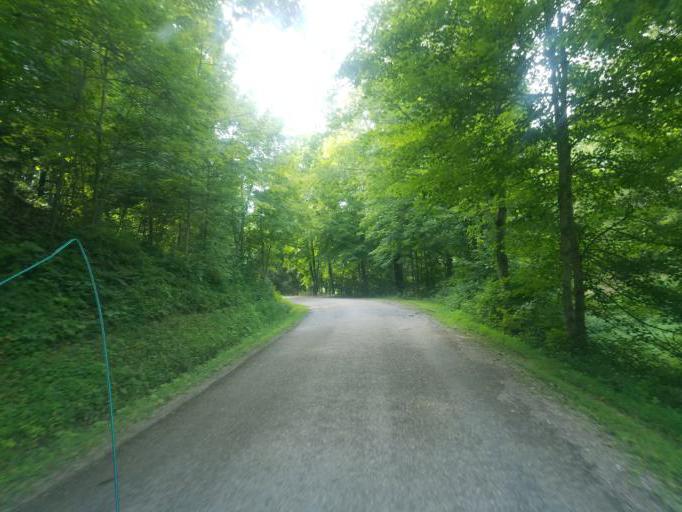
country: US
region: Ohio
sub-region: Knox County
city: Oak Hill
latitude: 40.3910
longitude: -82.1631
